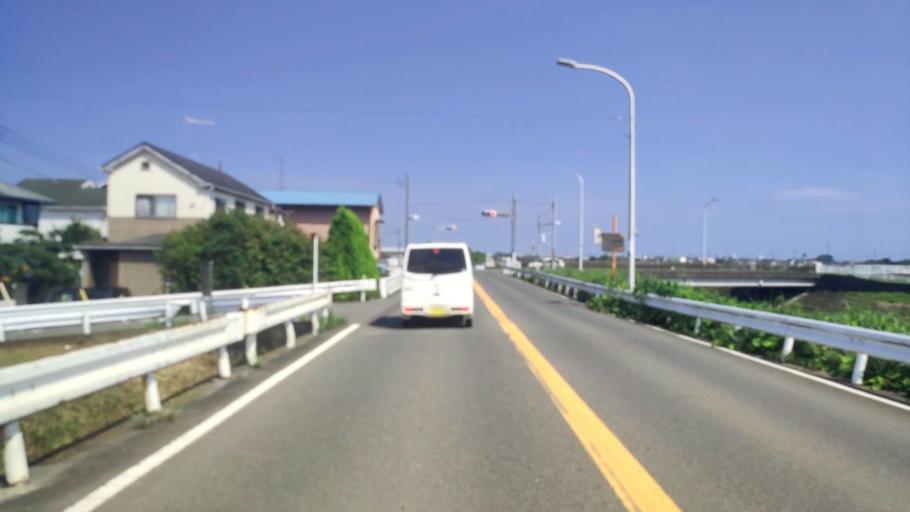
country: JP
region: Kanagawa
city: Isehara
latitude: 35.3675
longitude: 139.3164
